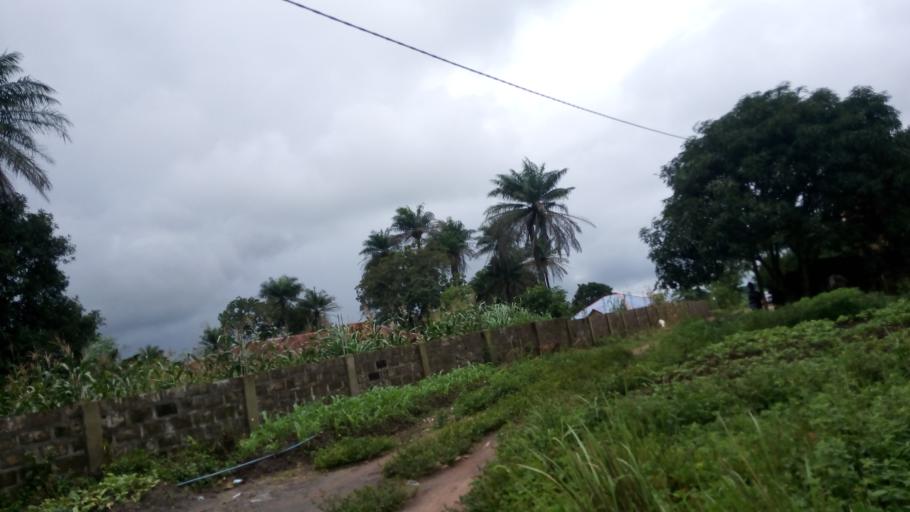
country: SL
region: Northern Province
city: Lunsar
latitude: 8.6927
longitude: -12.5281
